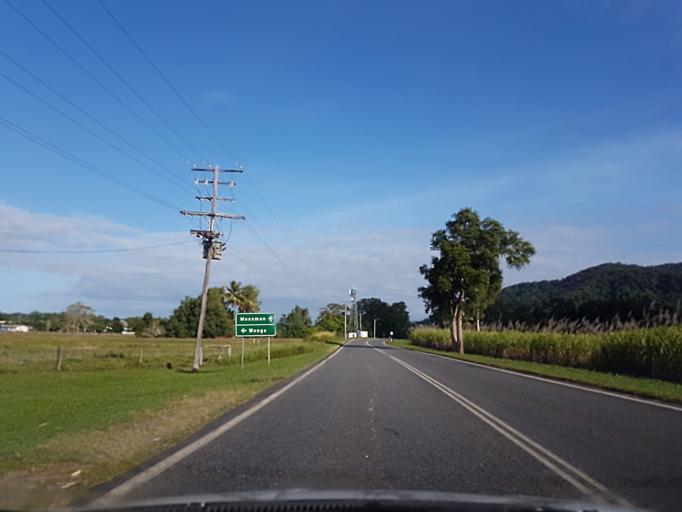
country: AU
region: Queensland
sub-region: Cairns
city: Port Douglas
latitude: -16.3444
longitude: 145.4091
